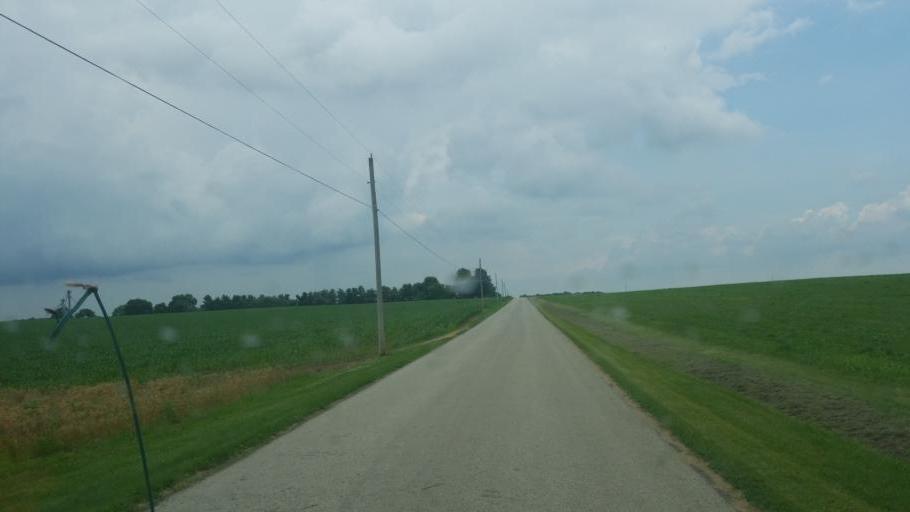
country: US
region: Ohio
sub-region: Wayne County
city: Wooster
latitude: 40.8872
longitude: -81.9785
